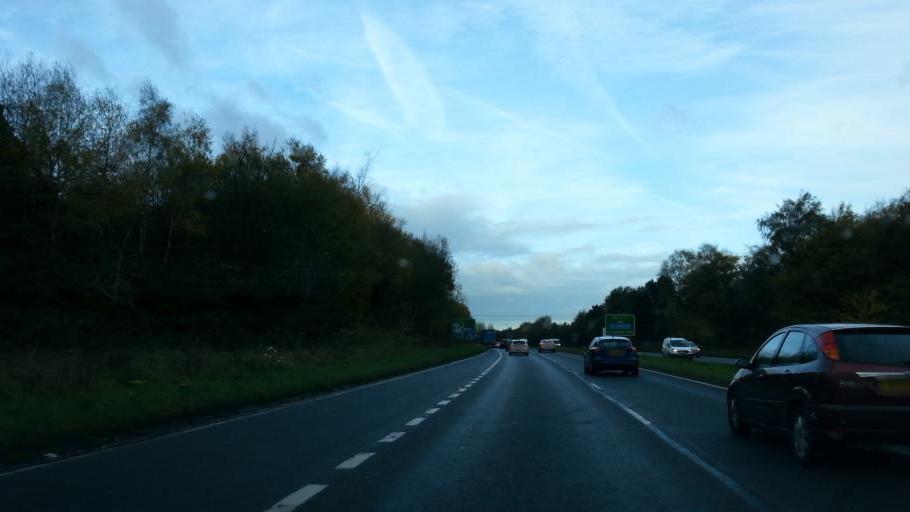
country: GB
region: England
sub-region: Leicestershire
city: Markfield
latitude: 52.6948
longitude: -1.2846
